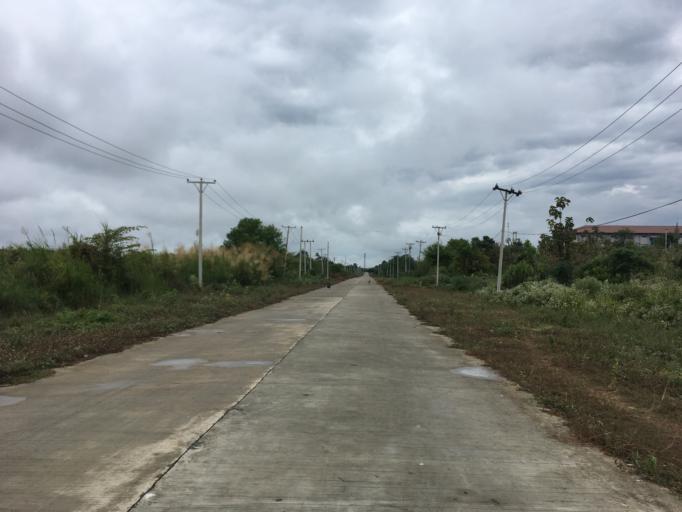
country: MM
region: Mandalay
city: Nay Pyi Taw
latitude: 19.6982
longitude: 96.1194
